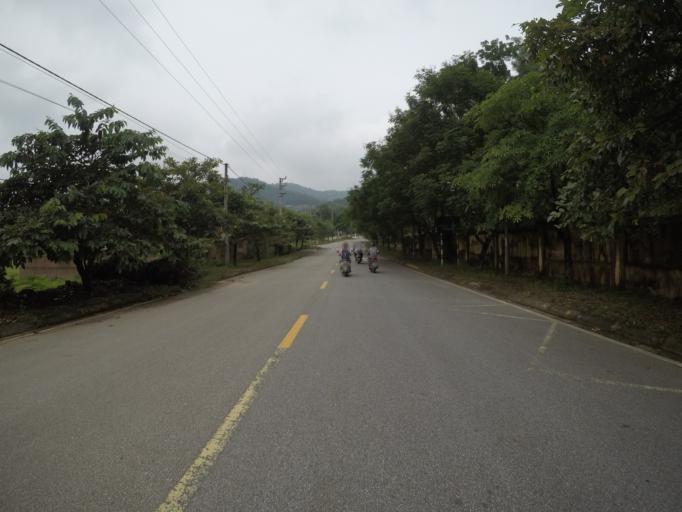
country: VN
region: Ha Noi
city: Soc Son
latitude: 21.2863
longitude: 105.8353
